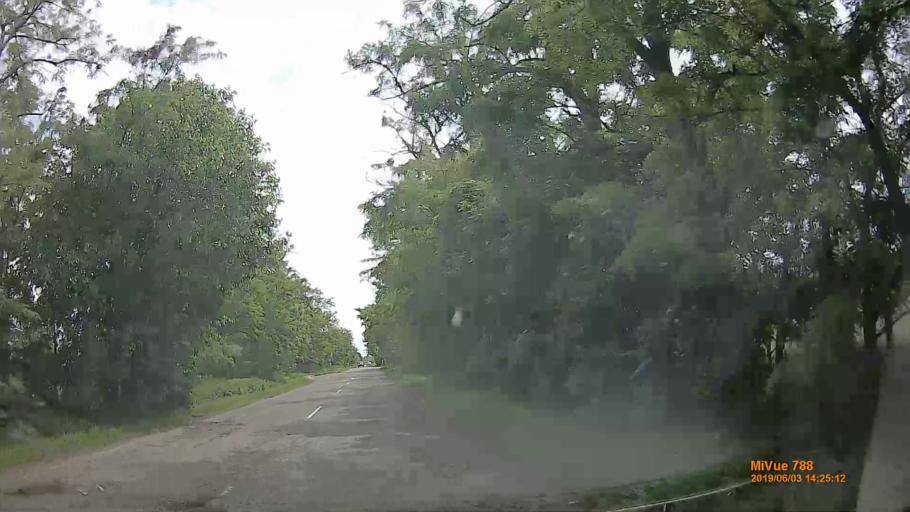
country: HU
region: Pest
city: Jaszkarajeno
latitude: 47.0064
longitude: 20.1260
